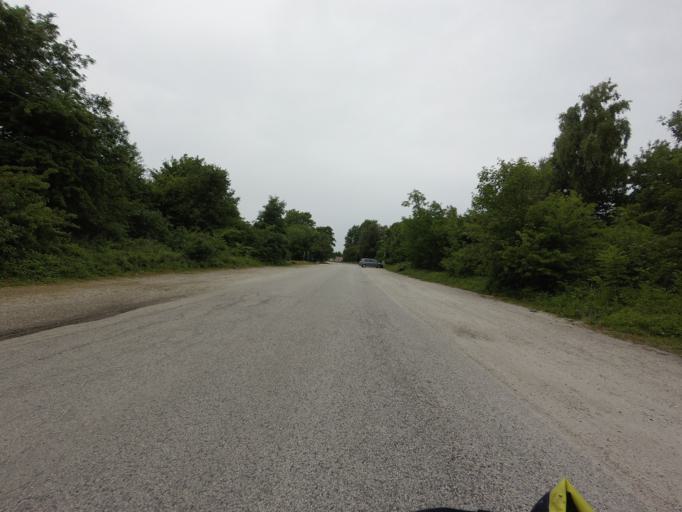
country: SE
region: Skane
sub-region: Malmo
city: Bunkeflostrand
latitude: 55.5240
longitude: 12.8986
